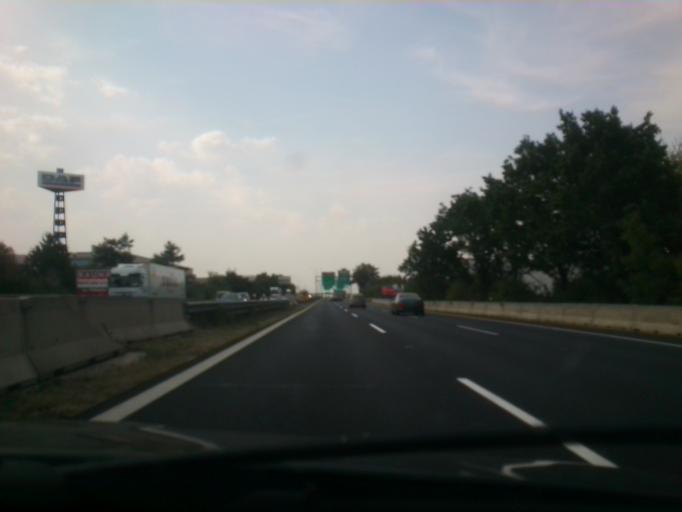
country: CZ
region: Central Bohemia
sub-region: Okres Praha-Vychod
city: Ricany
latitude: 49.9657
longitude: 14.6246
